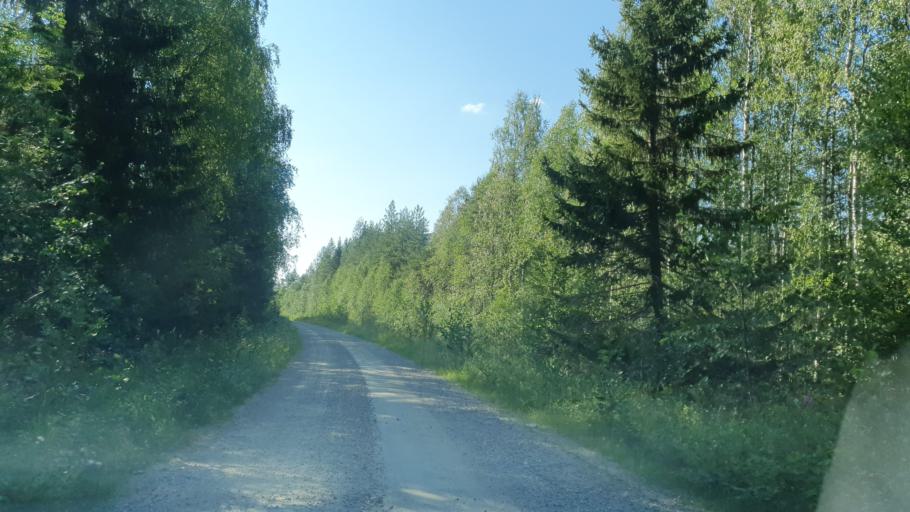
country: FI
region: Kainuu
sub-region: Kehys-Kainuu
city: Kuhmo
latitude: 64.0164
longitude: 29.7640
